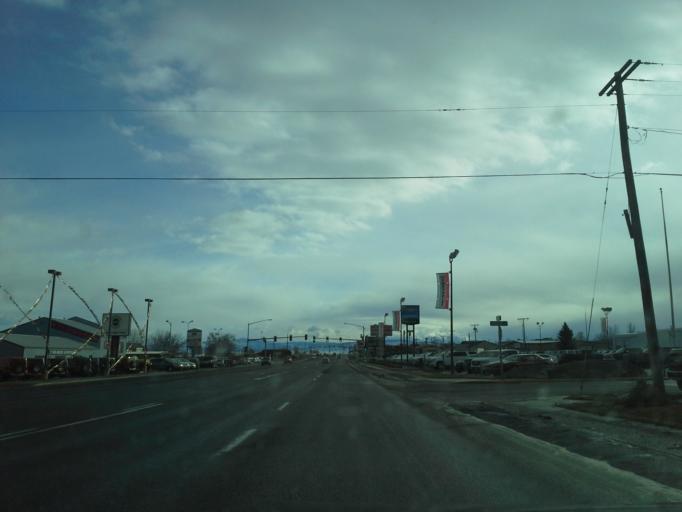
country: US
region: Montana
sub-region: Lewis and Clark County
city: Helena
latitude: 46.6067
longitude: -112.0155
